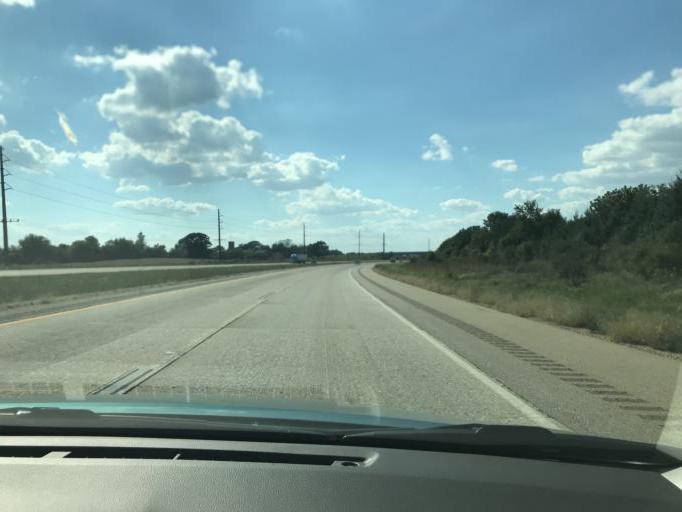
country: US
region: Wisconsin
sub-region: Walworth County
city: Delavan
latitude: 42.6127
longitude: -88.6424
